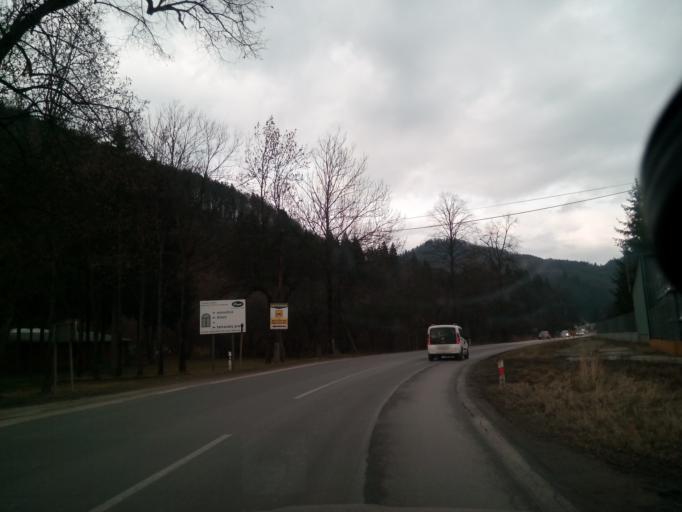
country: SK
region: Zilinsky
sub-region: Okres Dolny Kubin
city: Dolny Kubin
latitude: 49.2461
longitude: 19.3377
